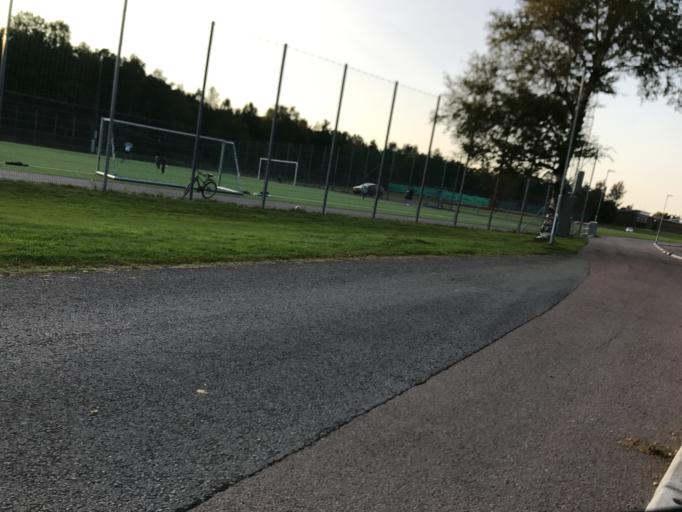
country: SE
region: Vaestra Goetaland
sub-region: Goteborg
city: Majorna
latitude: 57.7312
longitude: 11.8864
